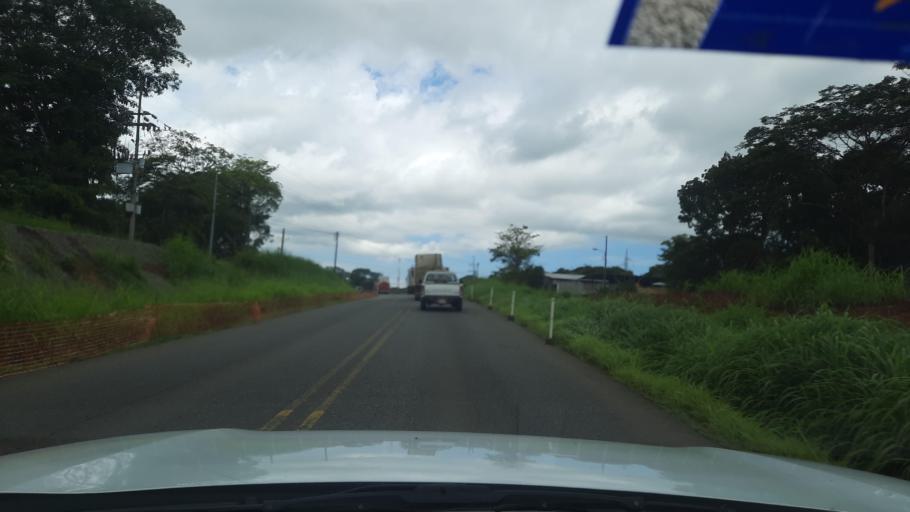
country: CR
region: Puntarenas
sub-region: Canton Central de Puntarenas
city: Puntarenas
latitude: 10.1142
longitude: -84.8939
